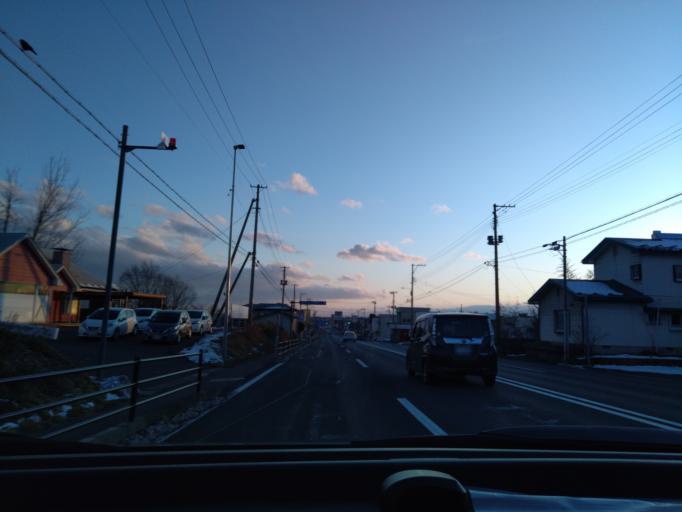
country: JP
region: Iwate
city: Hanamaki
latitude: 39.4210
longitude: 141.1288
